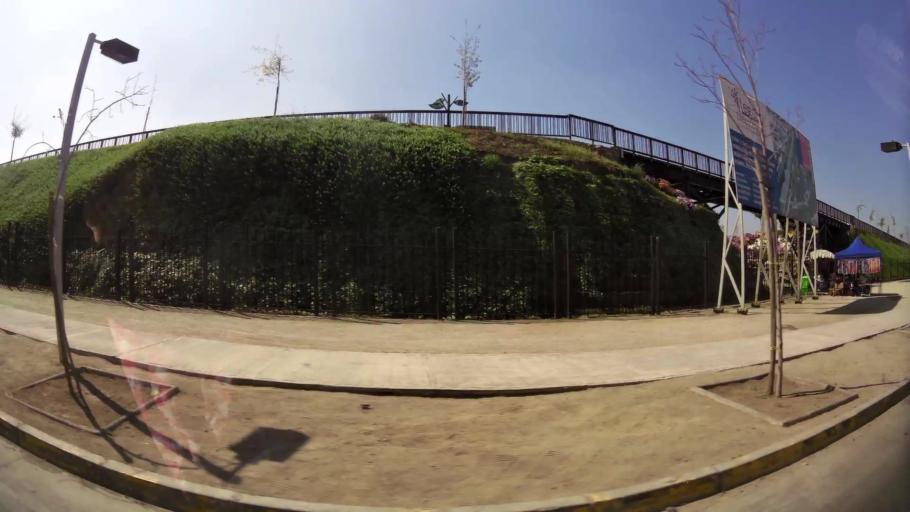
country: CL
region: Santiago Metropolitan
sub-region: Provincia de Santiago
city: Santiago
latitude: -33.4248
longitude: -70.6816
